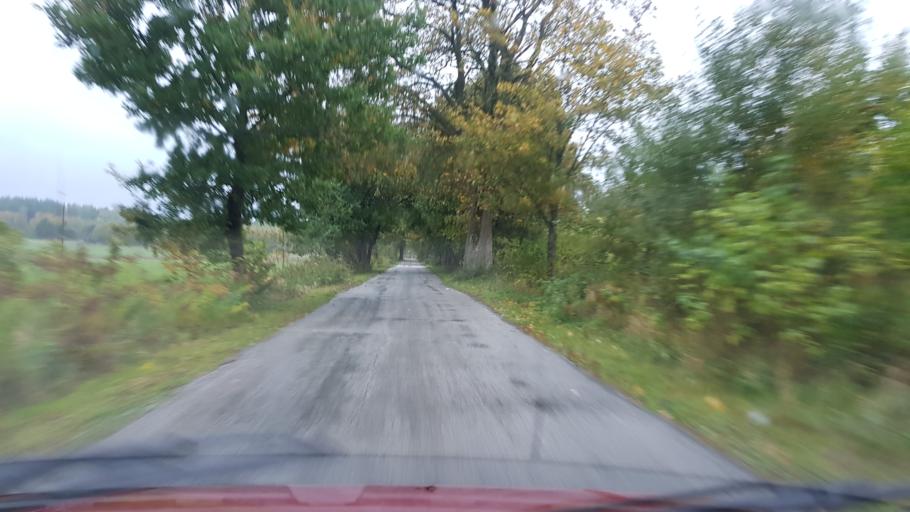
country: PL
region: West Pomeranian Voivodeship
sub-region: Koszalin
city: Koszalin
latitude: 54.1409
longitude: 16.1594
